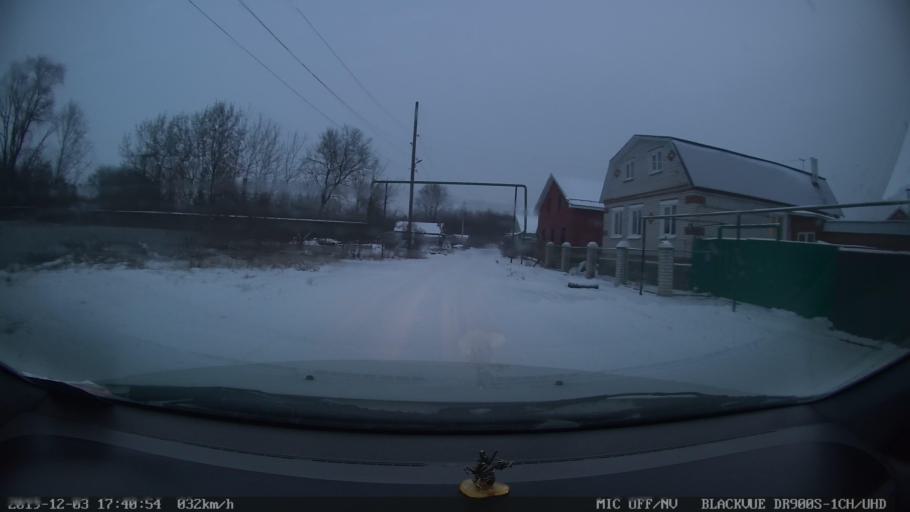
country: RU
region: Tatarstan
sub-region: Gorod Kazan'
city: Kazan
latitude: 55.7415
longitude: 49.1006
